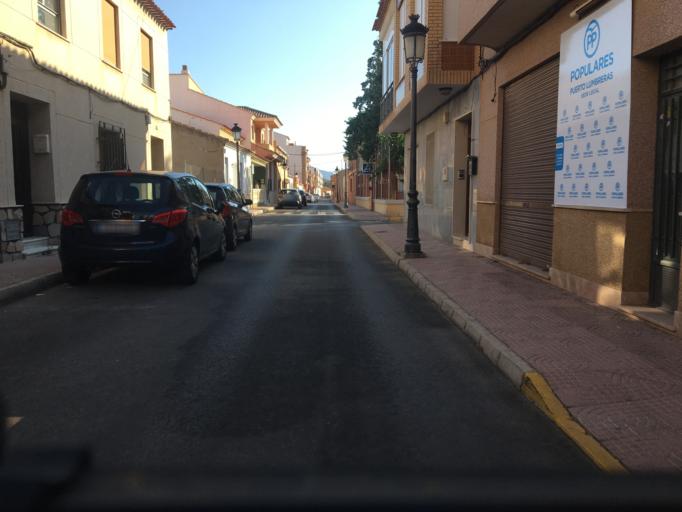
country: ES
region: Murcia
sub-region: Murcia
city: Puerto Lumbreras
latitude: 37.5646
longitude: -1.8087
